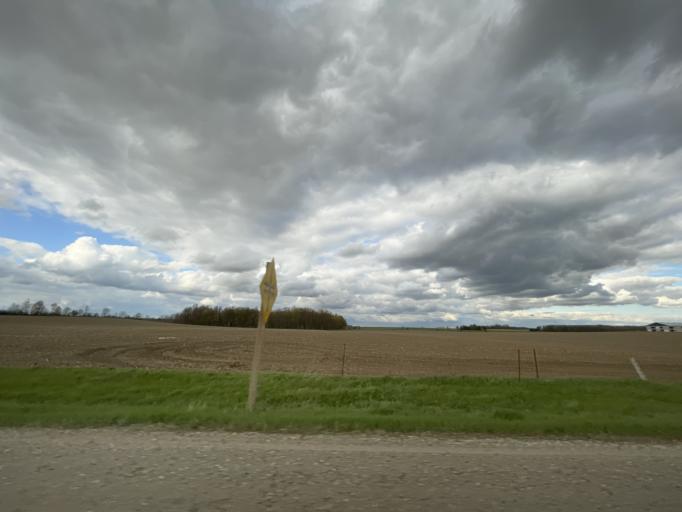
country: CA
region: Ontario
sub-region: Wellington County
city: Guelph
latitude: 43.5129
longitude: -80.3155
